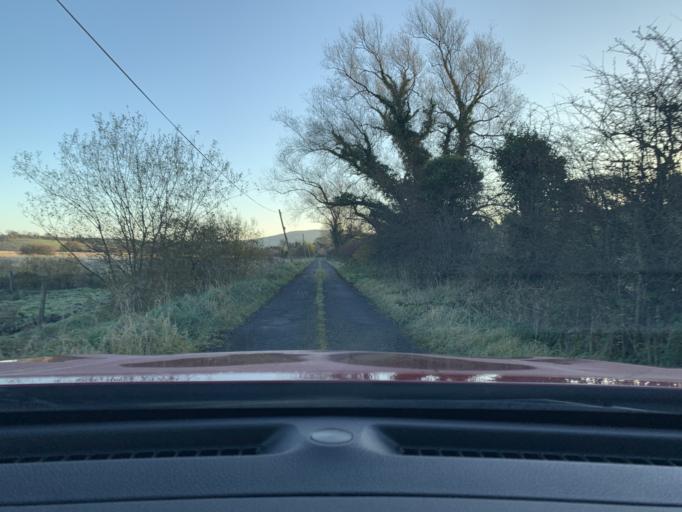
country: IE
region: Connaught
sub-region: Sligo
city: Ballymote
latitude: 54.0619
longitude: -8.5230
